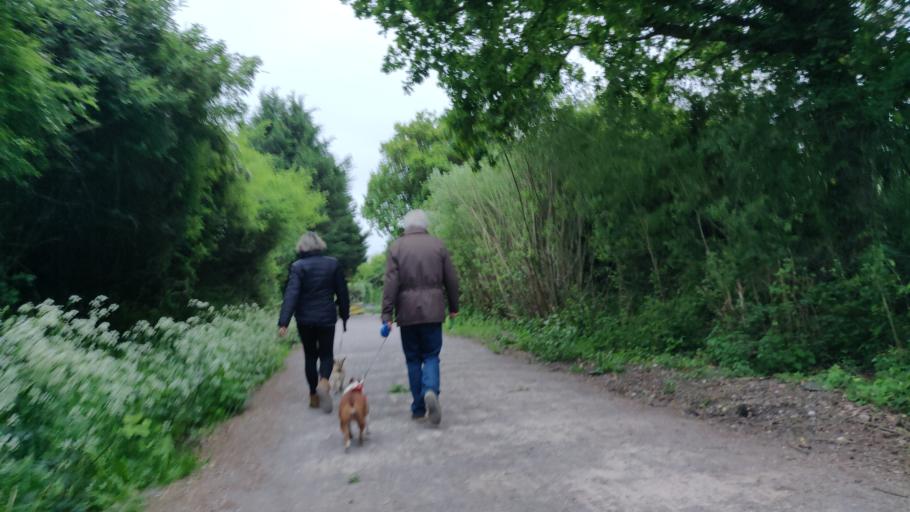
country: GB
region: England
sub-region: West Sussex
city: Partridge Green
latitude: 50.9598
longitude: -0.3102
